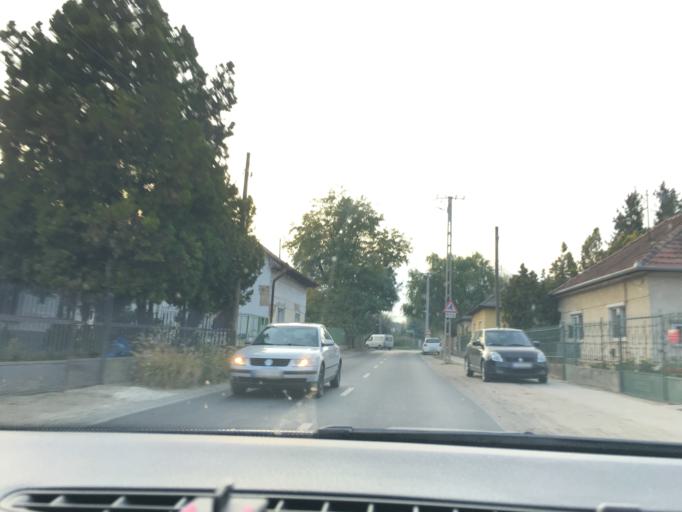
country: HU
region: Szabolcs-Szatmar-Bereg
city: Nagykallo
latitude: 47.8726
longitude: 21.8451
